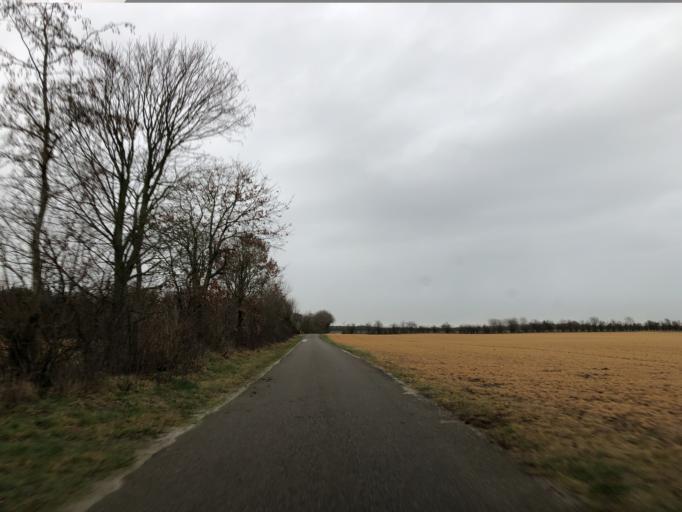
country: DK
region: Central Jutland
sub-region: Holstebro Kommune
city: Vinderup
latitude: 56.3766
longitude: 8.8558
